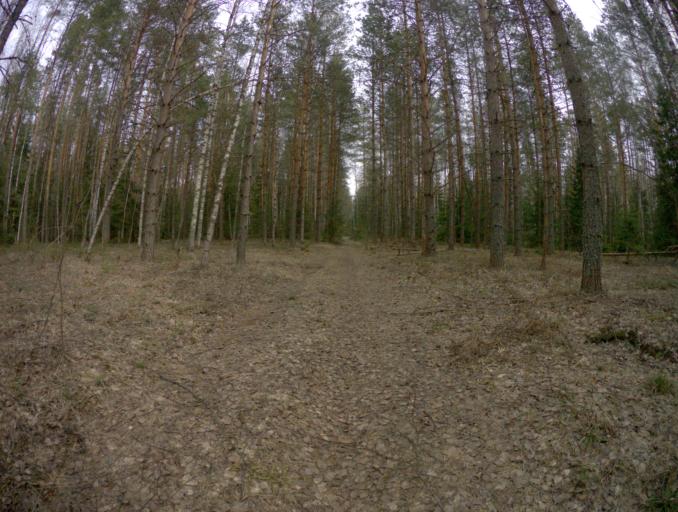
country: RU
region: Vladimir
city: Raduzhnyy
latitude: 55.9315
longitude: 40.2642
